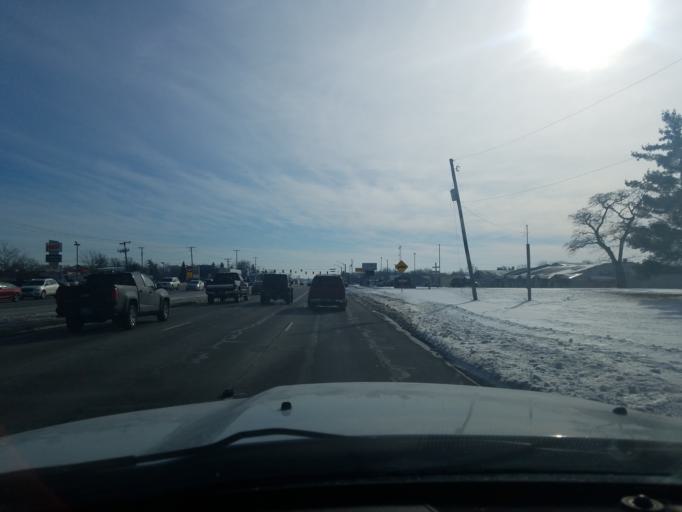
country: US
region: Indiana
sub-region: Allen County
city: Fort Wayne
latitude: 41.1576
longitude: -85.1656
